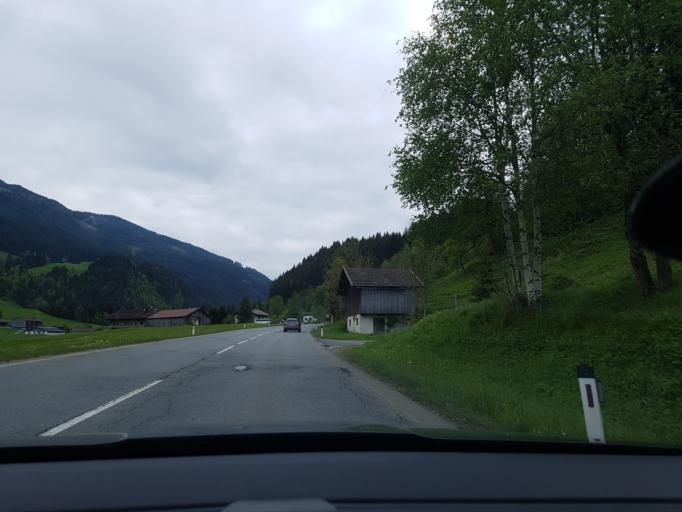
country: AT
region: Tyrol
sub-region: Politischer Bezirk Kitzbuhel
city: Jochberg
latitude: 47.3590
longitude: 12.4139
